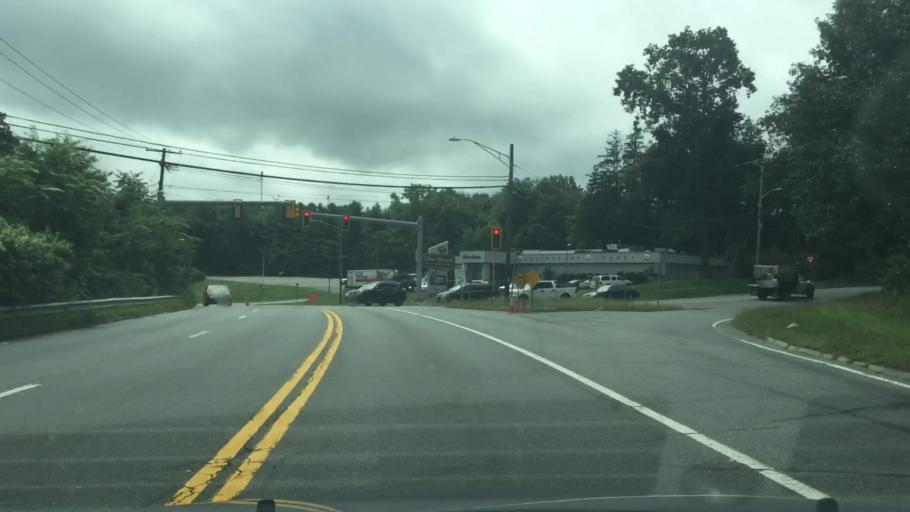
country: US
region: Massachusetts
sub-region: Essex County
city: North Andover
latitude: 42.7122
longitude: -71.1190
